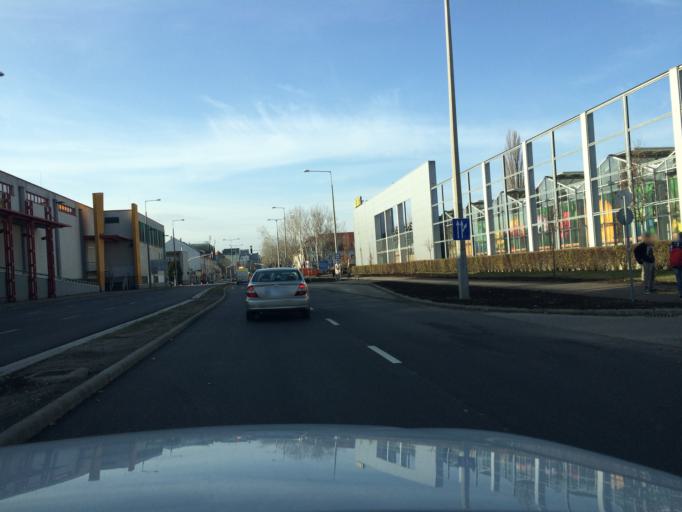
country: HU
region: Szabolcs-Szatmar-Bereg
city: Nyiregyhaza
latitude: 47.9566
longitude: 21.7276
